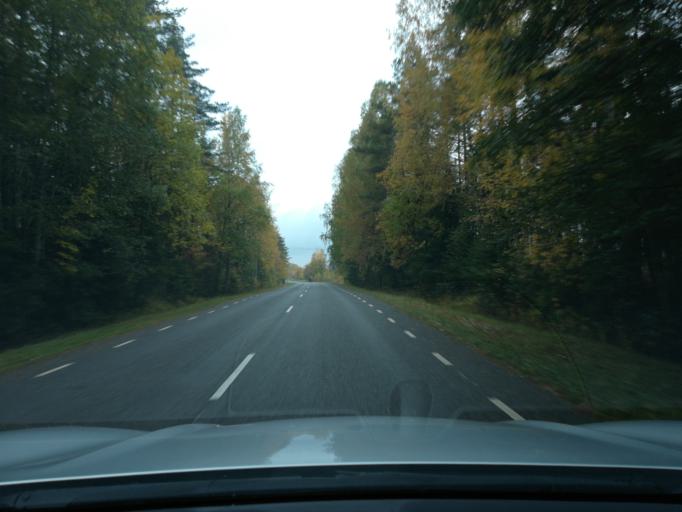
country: EE
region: Ida-Virumaa
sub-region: Johvi vald
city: Johvi
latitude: 59.0801
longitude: 27.3281
